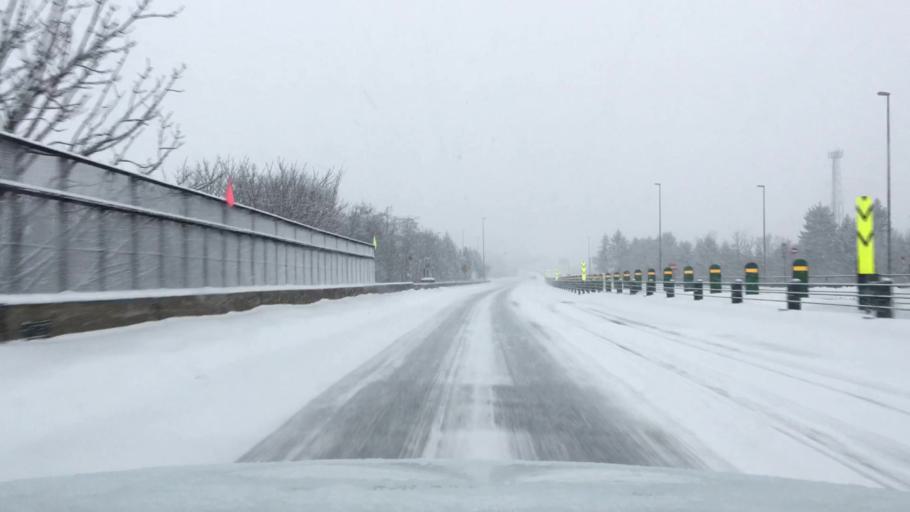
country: JP
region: Akita
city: Hanawa
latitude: 40.2551
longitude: 140.7662
